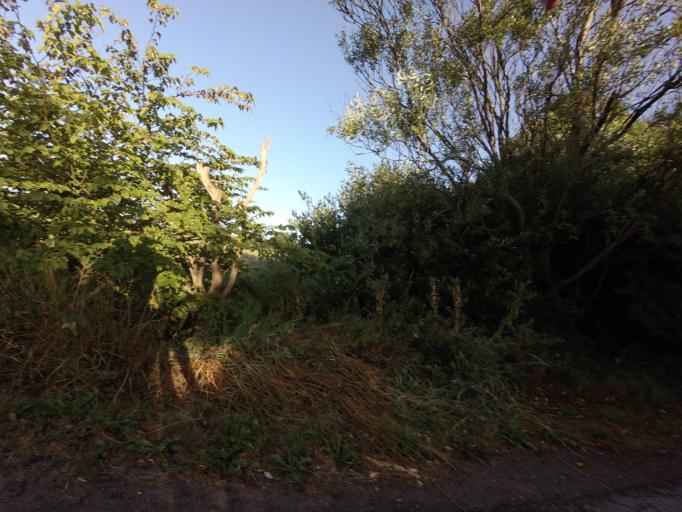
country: DK
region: North Denmark
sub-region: Hjorring Kommune
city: Vra
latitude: 57.3673
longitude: 9.8654
